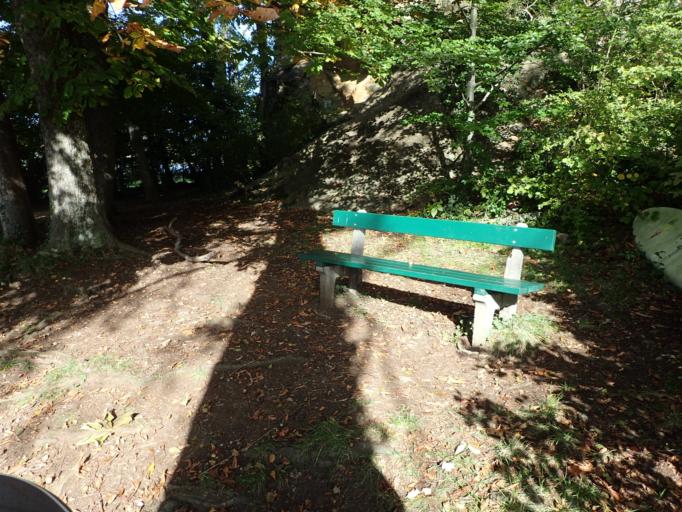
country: AT
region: Salzburg
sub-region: Politischer Bezirk Salzburg-Umgebung
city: Mattsee
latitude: 47.9692
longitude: 13.0937
